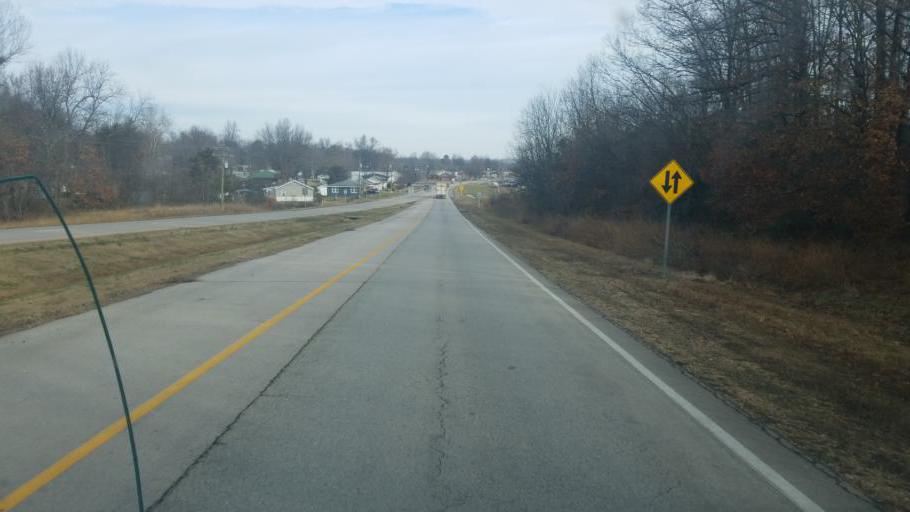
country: US
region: Missouri
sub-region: Stoddard County
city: Bloomfield
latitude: 36.8776
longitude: -89.9275
